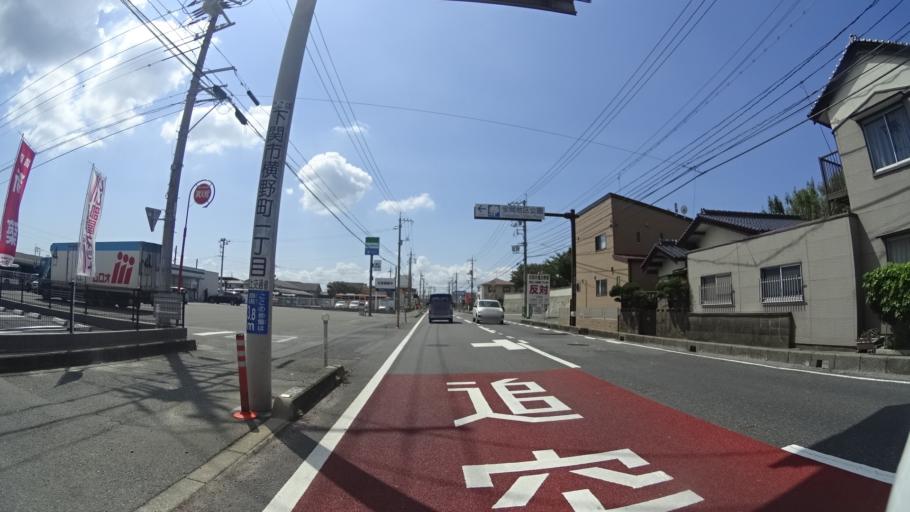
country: JP
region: Yamaguchi
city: Shimonoseki
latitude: 34.0327
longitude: 130.9127
